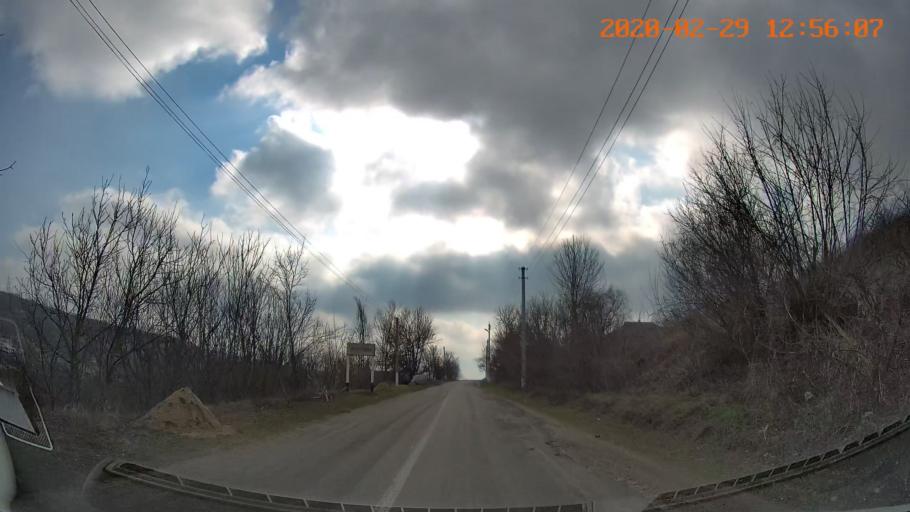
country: MD
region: Telenesti
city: Camenca
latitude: 48.0898
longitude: 28.7232
